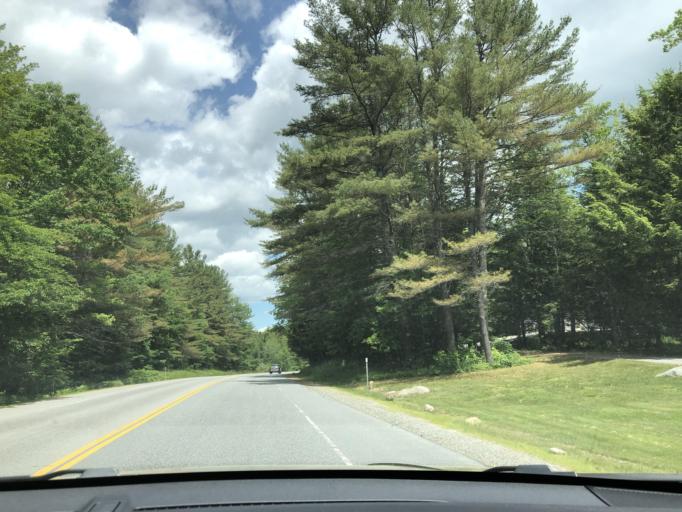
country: US
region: New Hampshire
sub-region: Merrimack County
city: New London
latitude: 43.4246
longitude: -72.0312
